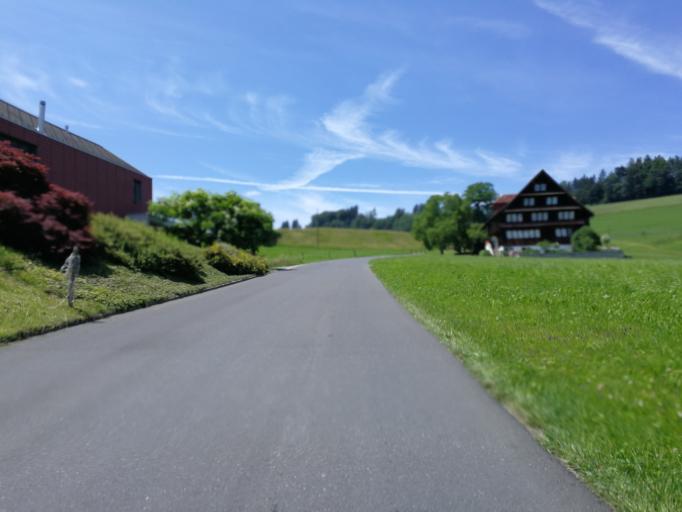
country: CH
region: Schwyz
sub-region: Bezirk March
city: Tuggen
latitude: 47.2016
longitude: 8.9319
